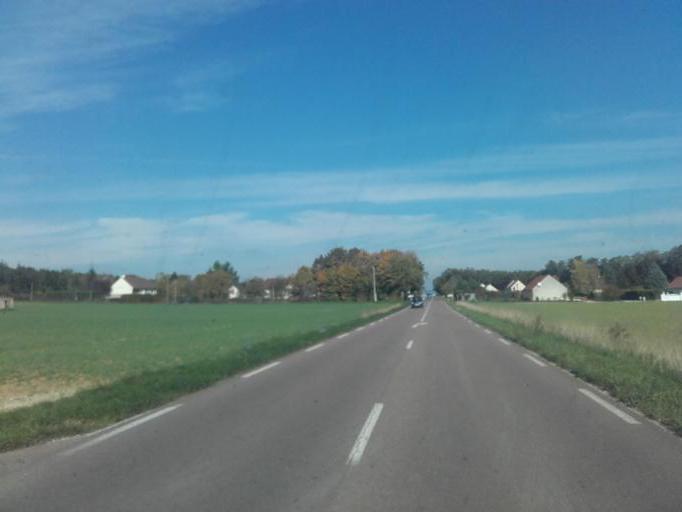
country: FR
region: Bourgogne
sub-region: Departement de Saone-et-Loire
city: Chagny
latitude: 46.8939
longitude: 4.7522
